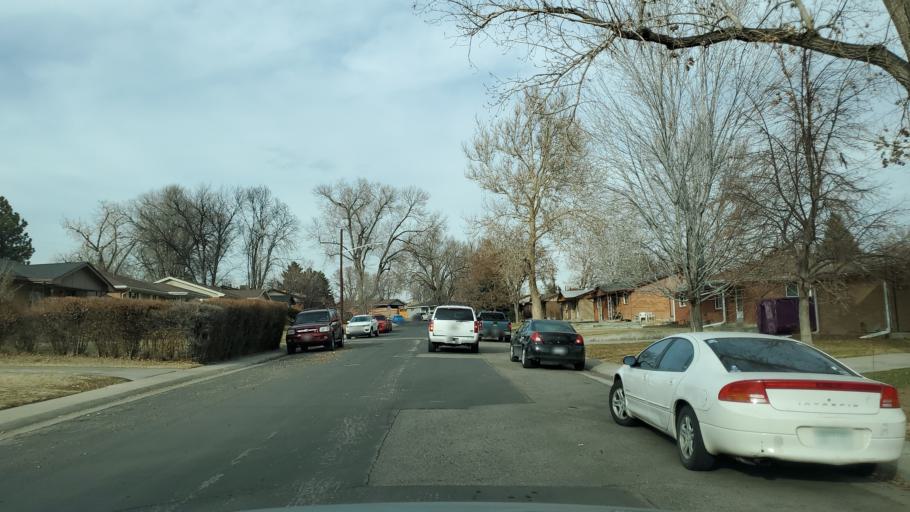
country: US
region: Colorado
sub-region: Adams County
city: Westminster
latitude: 39.8319
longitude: -105.0224
